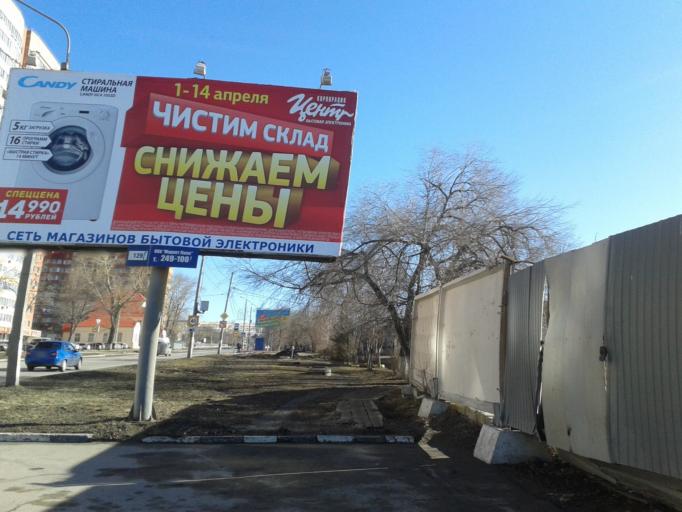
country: RU
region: Ulyanovsk
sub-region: Ulyanovskiy Rayon
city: Ulyanovsk
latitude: 54.3002
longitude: 48.3828
